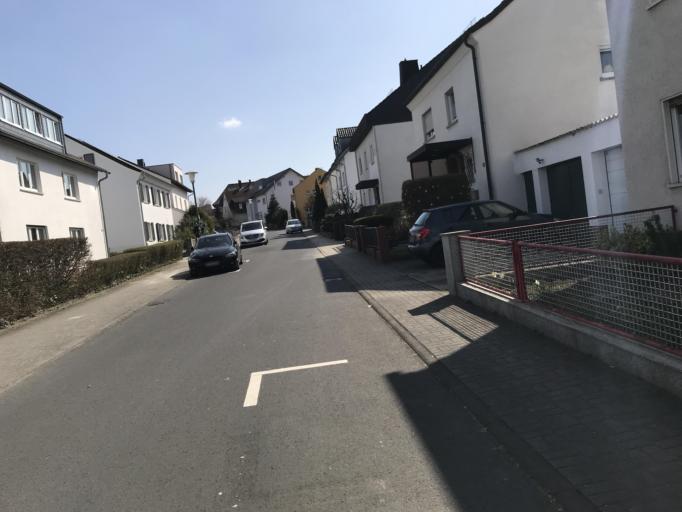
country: DE
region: Hesse
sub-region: Regierungsbezirk Kassel
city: Fulda
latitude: 50.5543
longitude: 9.6915
